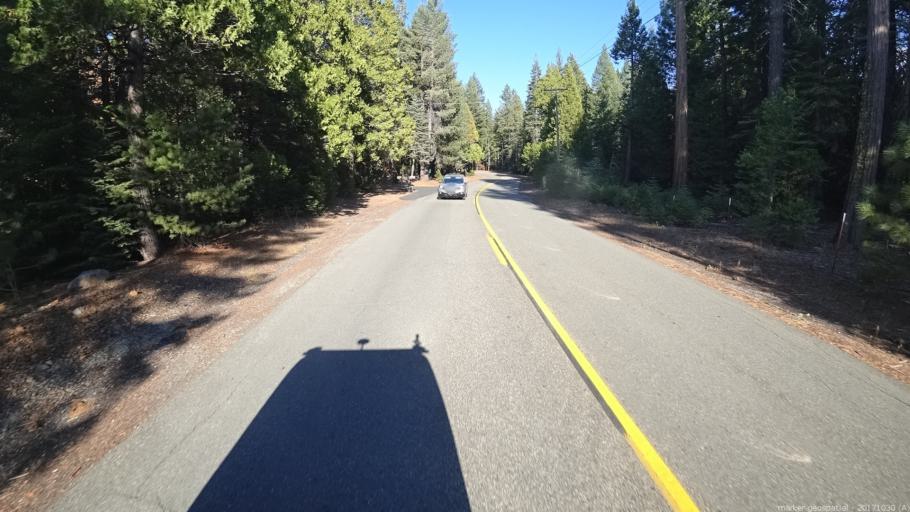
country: US
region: California
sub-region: Shasta County
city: Shingletown
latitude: 40.5205
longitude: -121.7518
